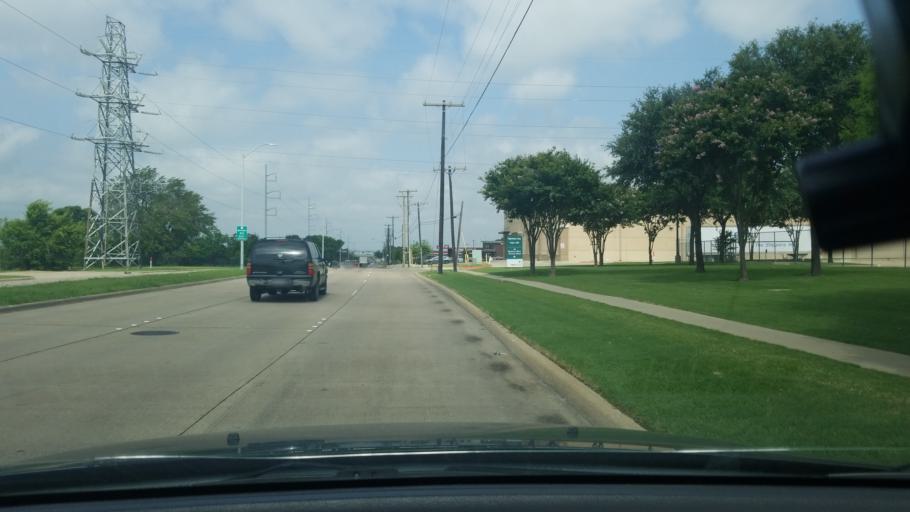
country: US
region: Texas
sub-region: Dallas County
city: Mesquite
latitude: 32.7925
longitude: -96.6819
